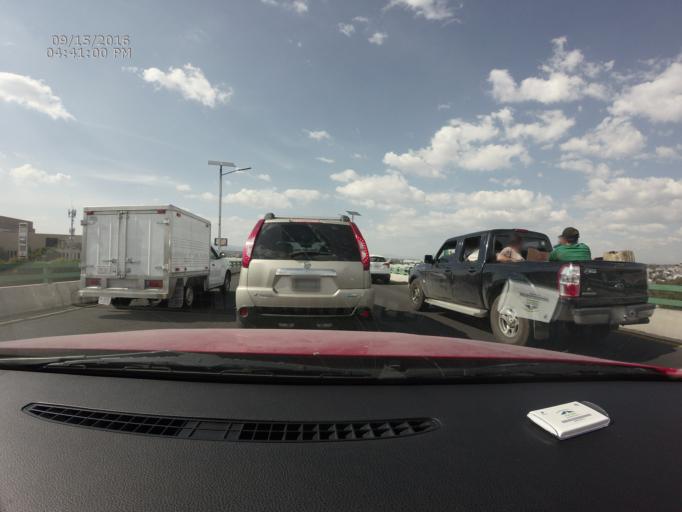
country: MX
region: Mexico
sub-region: Tultitlan
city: Buenavista
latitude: 19.6028
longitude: -99.1890
